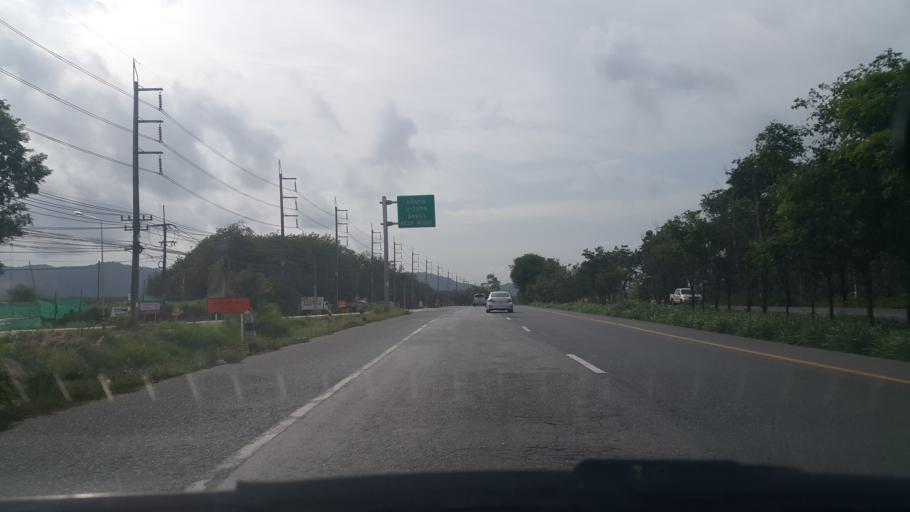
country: TH
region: Rayong
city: Nikhom Phattana
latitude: 12.7884
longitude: 101.1567
